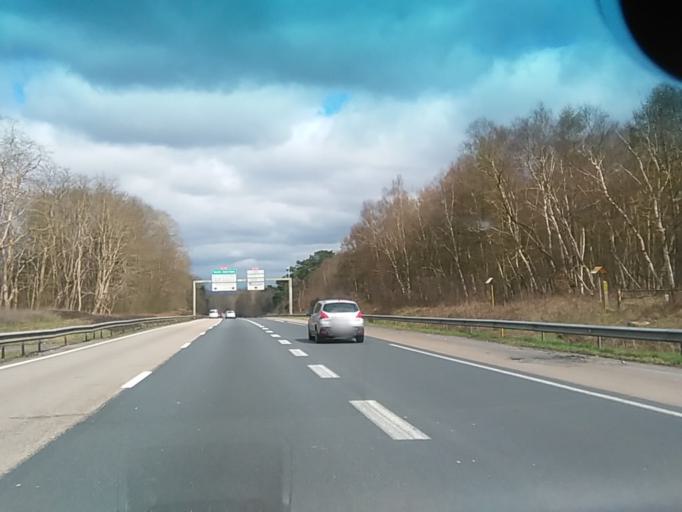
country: FR
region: Haute-Normandie
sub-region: Departement de la Seine-Maritime
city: Le Grand-Quevilly
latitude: 49.3728
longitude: 1.0446
